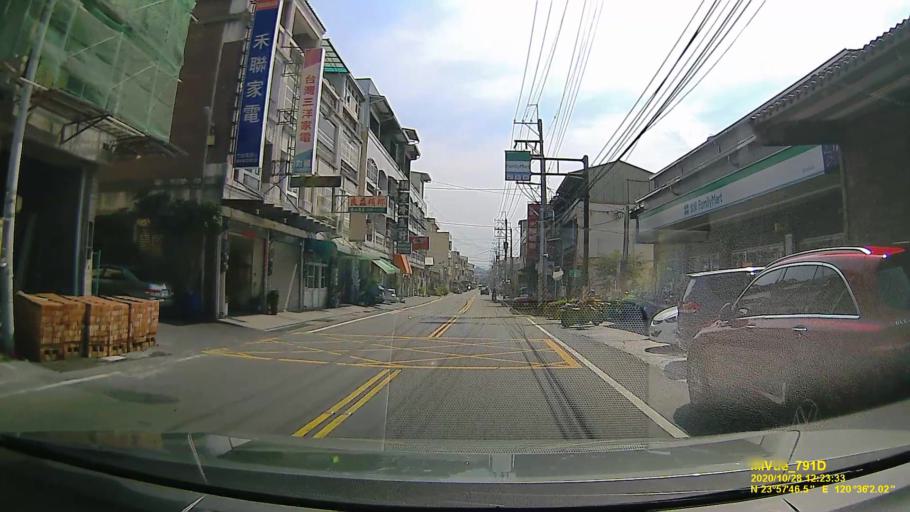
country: TW
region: Taiwan
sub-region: Nantou
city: Nantou
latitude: 23.9629
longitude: 120.6006
